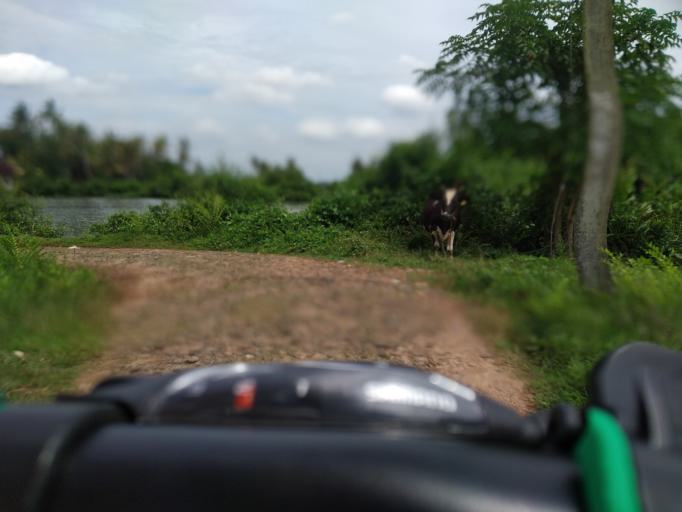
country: IN
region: Kerala
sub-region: Ernakulam
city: Elur
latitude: 10.0818
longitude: 76.2208
